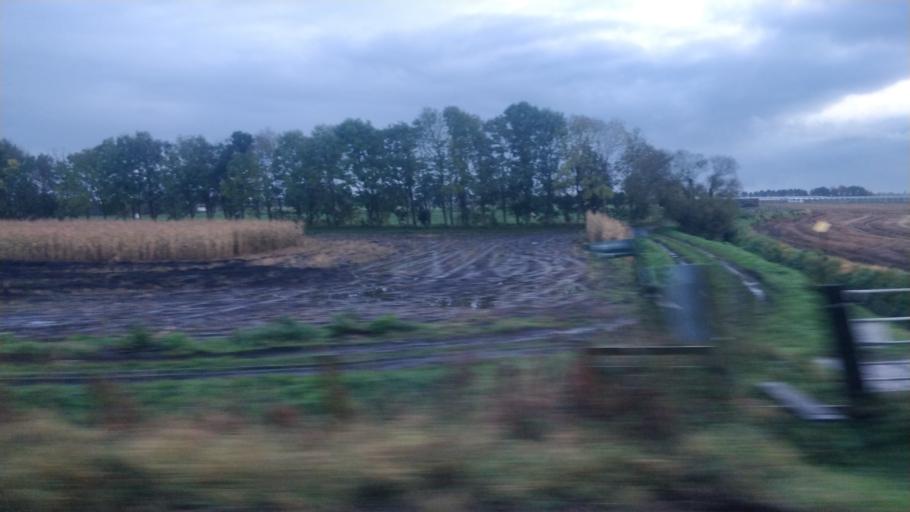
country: GB
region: England
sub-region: Lancashire
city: Ormskirk
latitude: 53.6158
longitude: -2.8831
